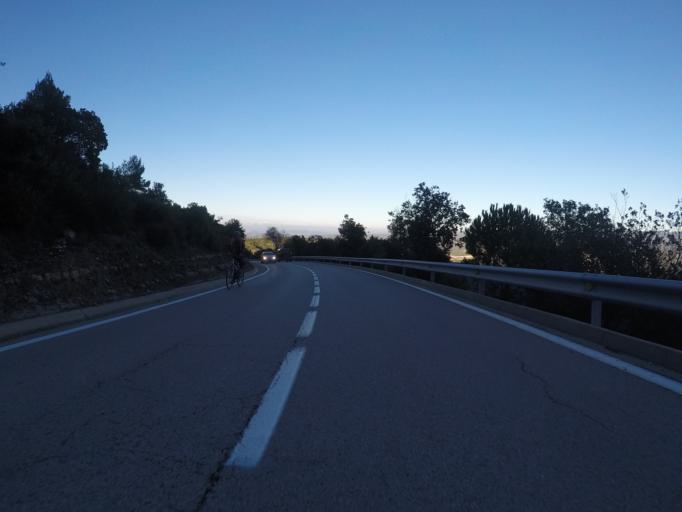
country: ES
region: Catalonia
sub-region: Provincia de Barcelona
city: Monistrol de Montserrat
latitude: 41.6121
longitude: 1.8230
